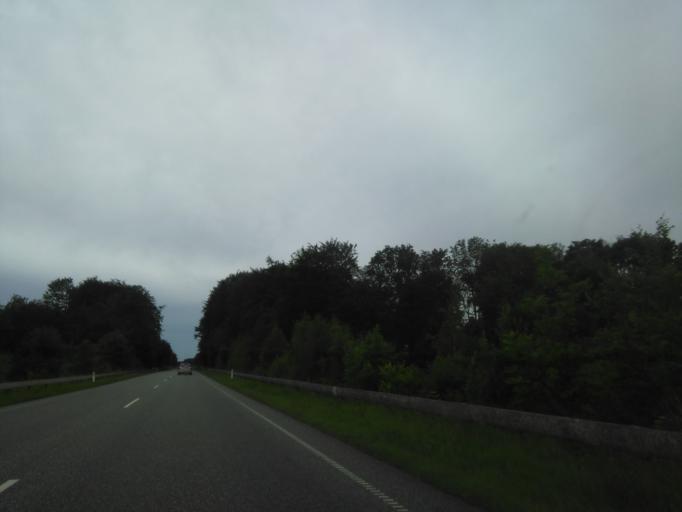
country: DK
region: Central Jutland
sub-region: Horsens Kommune
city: Horsens
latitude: 55.9146
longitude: 9.9174
